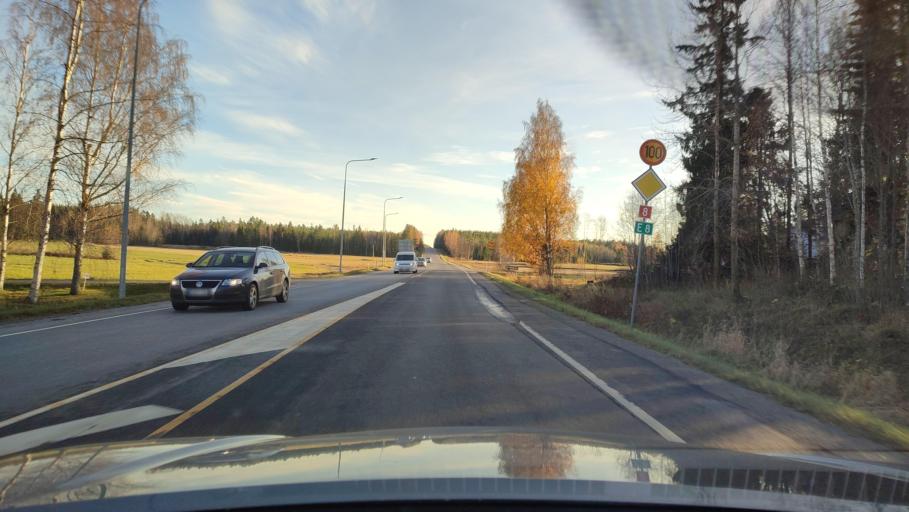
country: FI
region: Ostrobothnia
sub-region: Vaasa
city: Ristinummi
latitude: 63.0230
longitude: 21.7569
